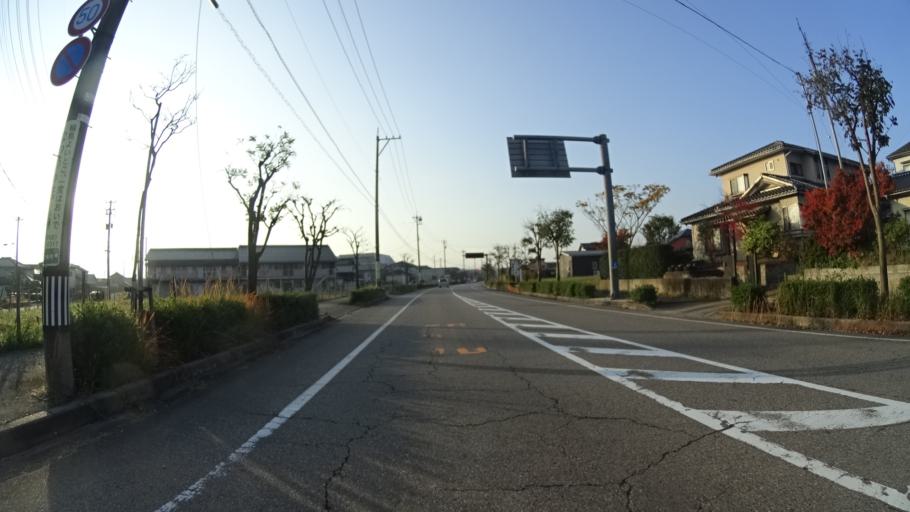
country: JP
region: Ishikawa
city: Nanao
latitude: 37.0826
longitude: 136.9263
